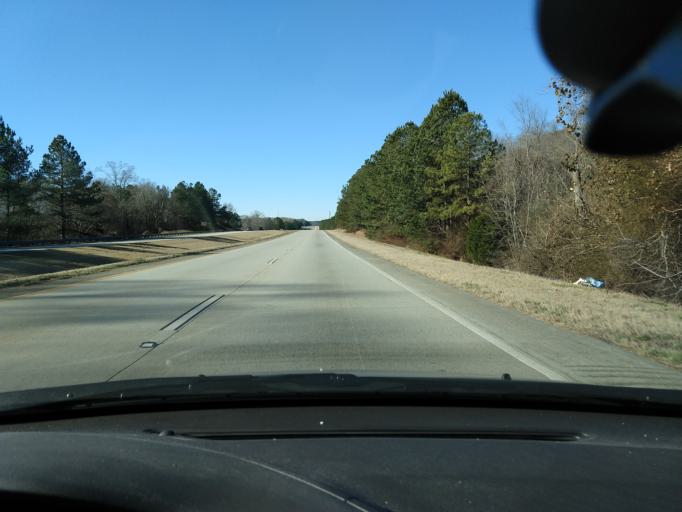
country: US
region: Georgia
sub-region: Barrow County
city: Russell
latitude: 33.9506
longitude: -83.6963
